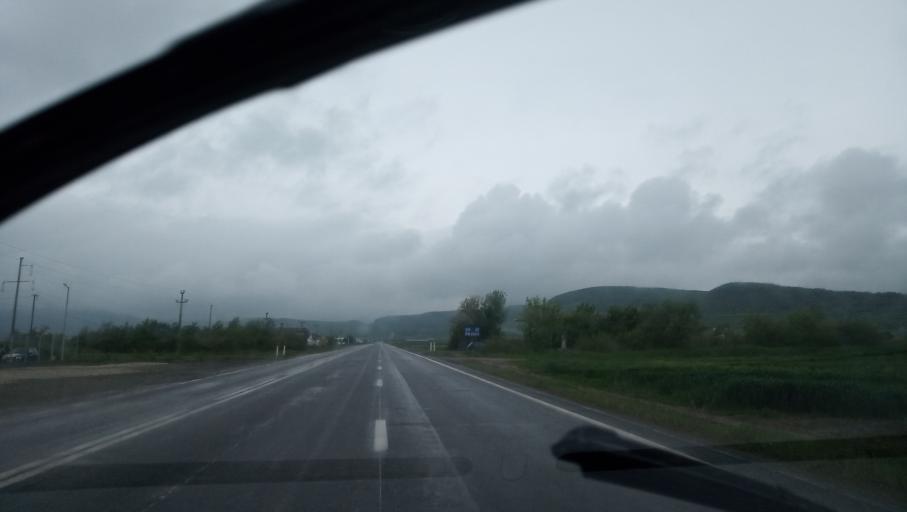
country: RO
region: Sibiu
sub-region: Comuna Cristian
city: Cristian
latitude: 45.7854
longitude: 24.0067
